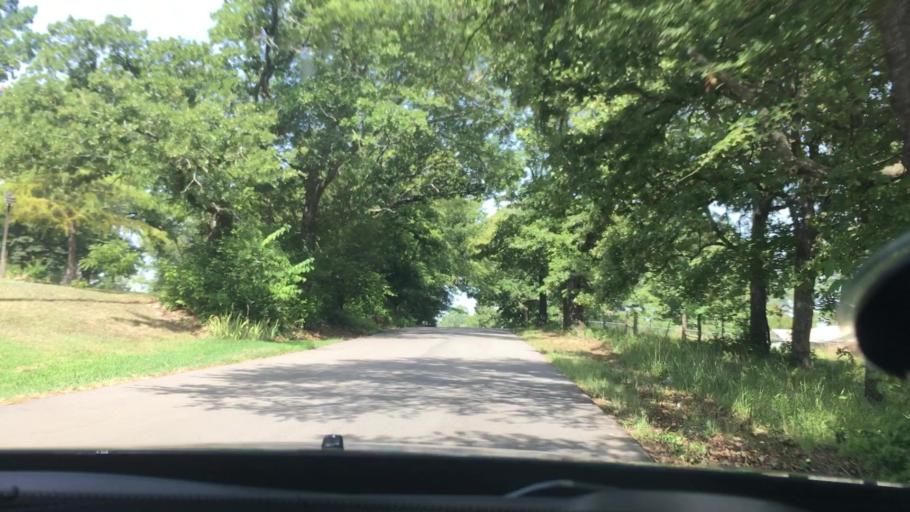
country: US
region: Oklahoma
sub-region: Atoka County
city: Atoka
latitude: 34.3603
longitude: -96.1575
